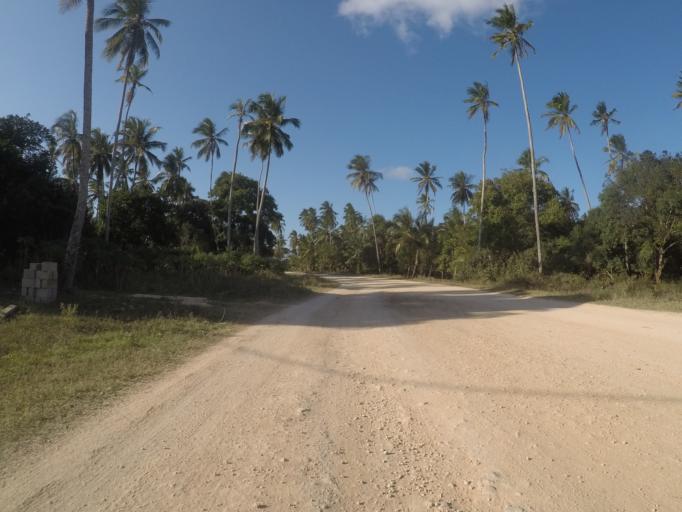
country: TZ
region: Zanzibar Central/South
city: Koani
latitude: -6.1638
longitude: 39.2870
